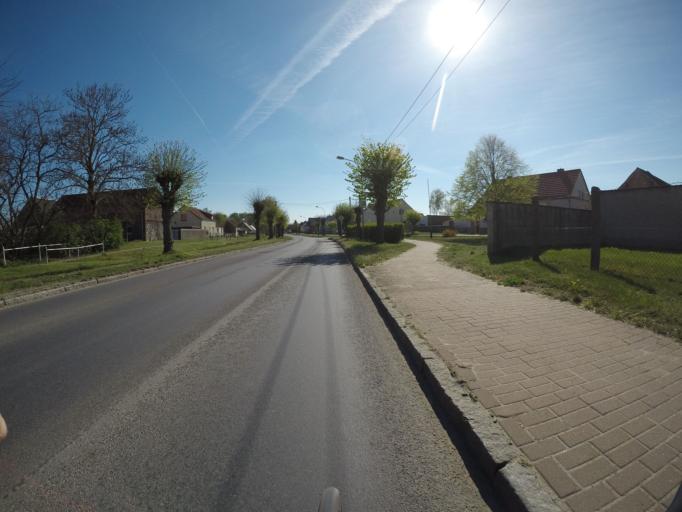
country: DE
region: Brandenburg
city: Rehfelde
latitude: 52.5008
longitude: 13.9224
